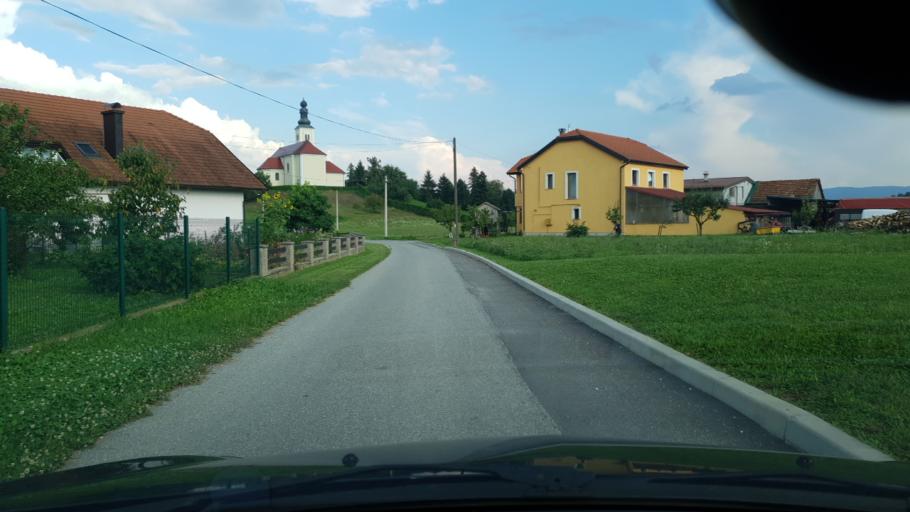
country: HR
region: Krapinsko-Zagorska
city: Zabok
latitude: 46.0814
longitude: 15.9031
